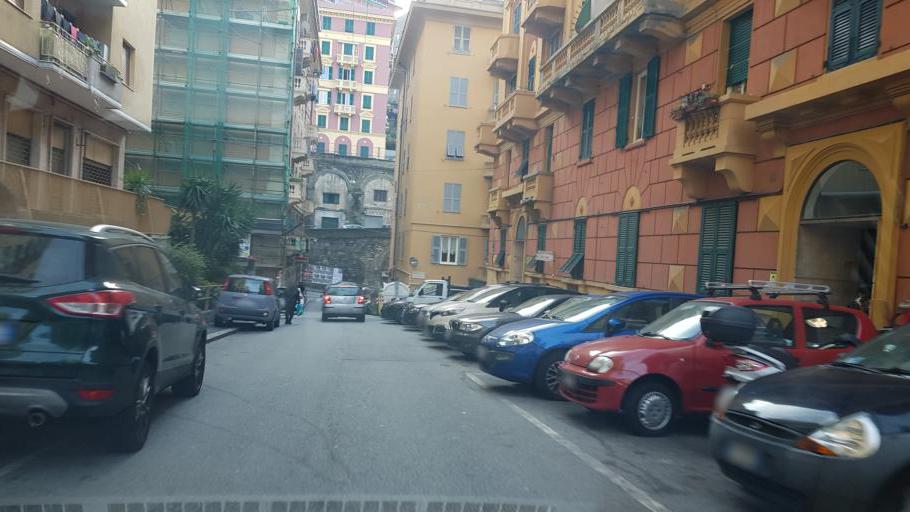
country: IT
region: Liguria
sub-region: Provincia di Genova
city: San Teodoro
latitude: 44.4161
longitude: 8.8909
